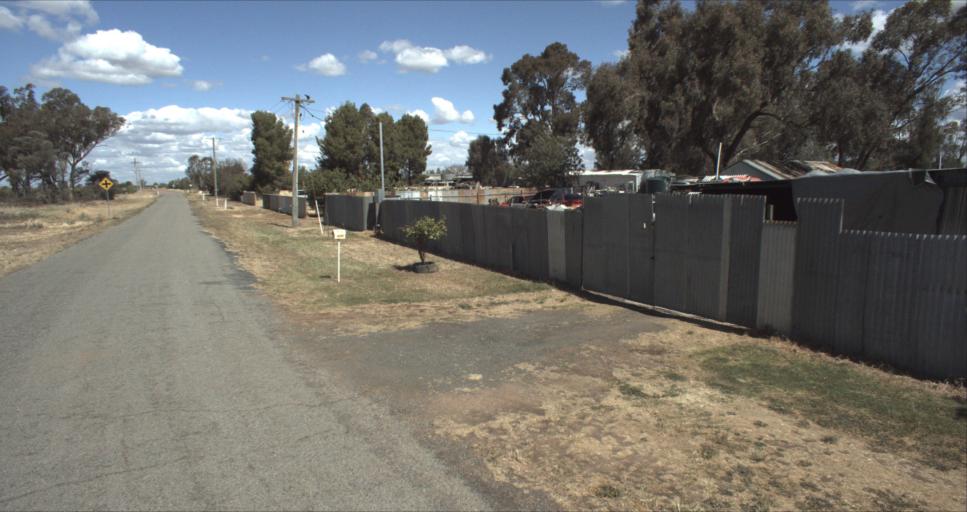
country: AU
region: New South Wales
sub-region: Leeton
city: Leeton
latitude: -34.5164
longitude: 146.2339
